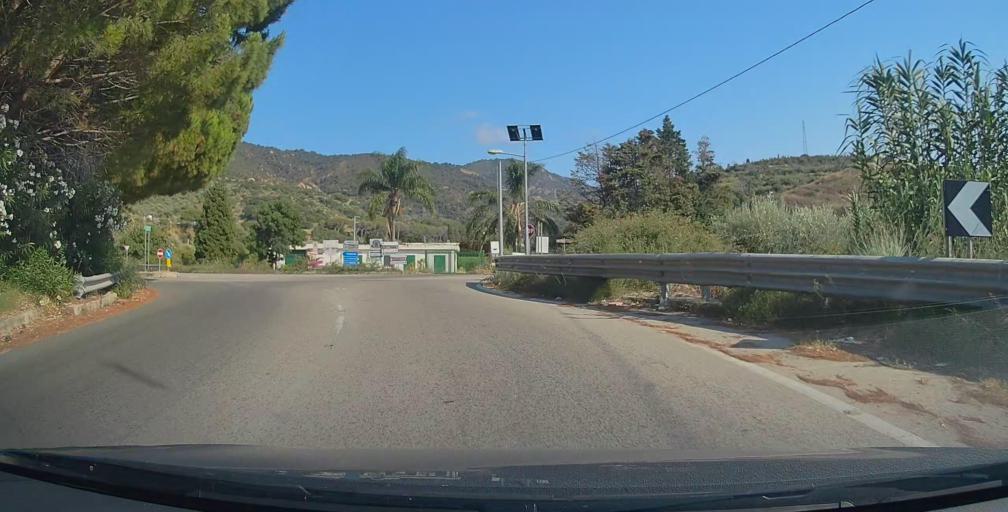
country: IT
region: Sicily
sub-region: Messina
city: Patti
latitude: 38.1374
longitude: 14.9969
